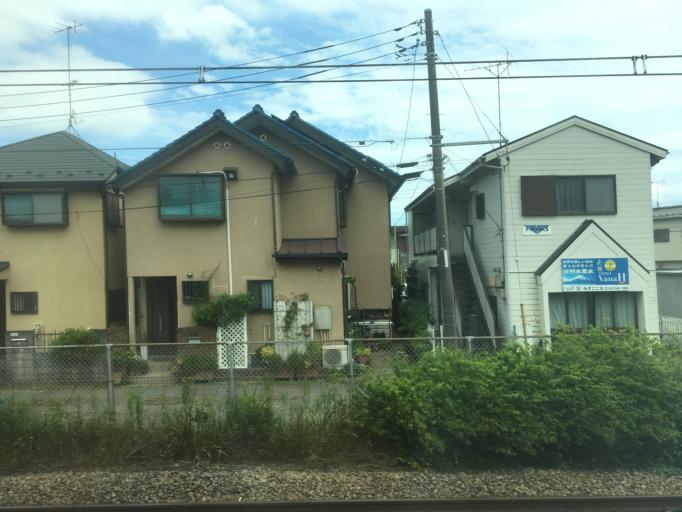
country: JP
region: Tokyo
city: Hino
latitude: 35.6617
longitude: 139.3849
